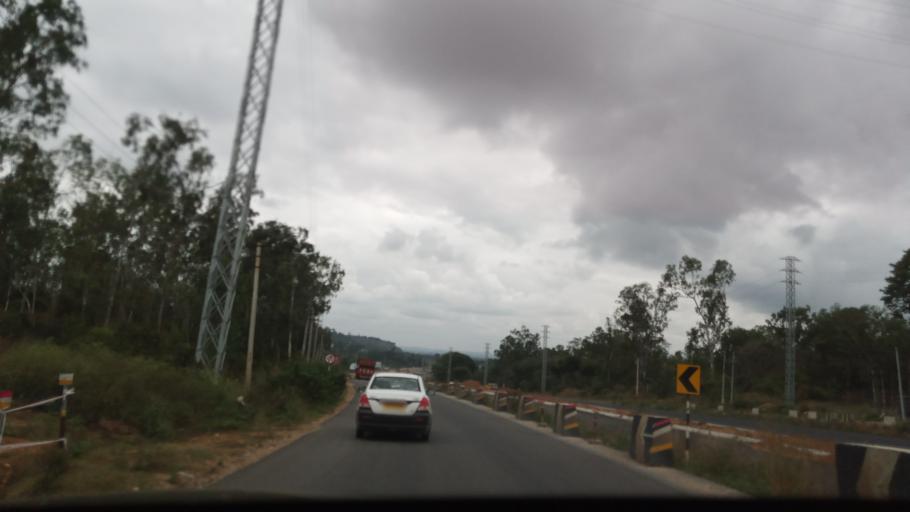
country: IN
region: Karnataka
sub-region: Mandya
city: Shrirangapattana
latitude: 12.4529
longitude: 76.7396
